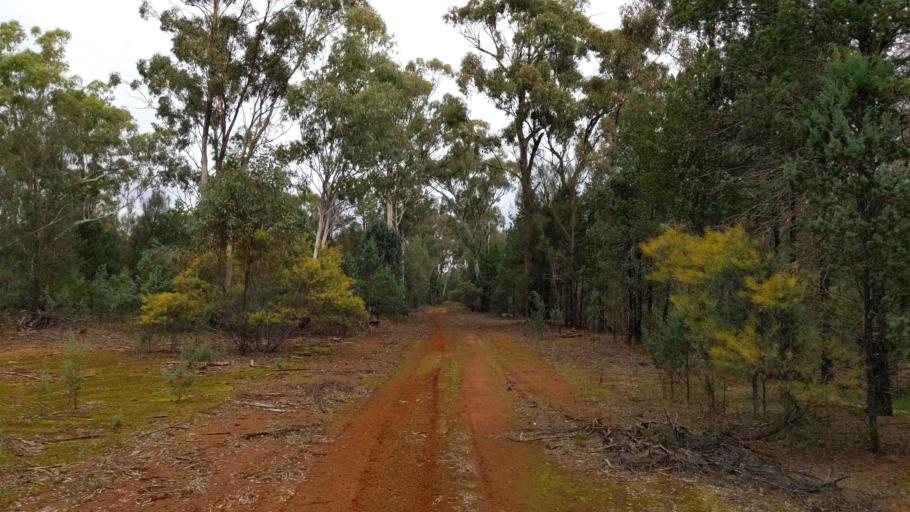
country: AU
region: New South Wales
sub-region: Coolamon
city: Coolamon
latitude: -34.8405
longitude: 146.9337
